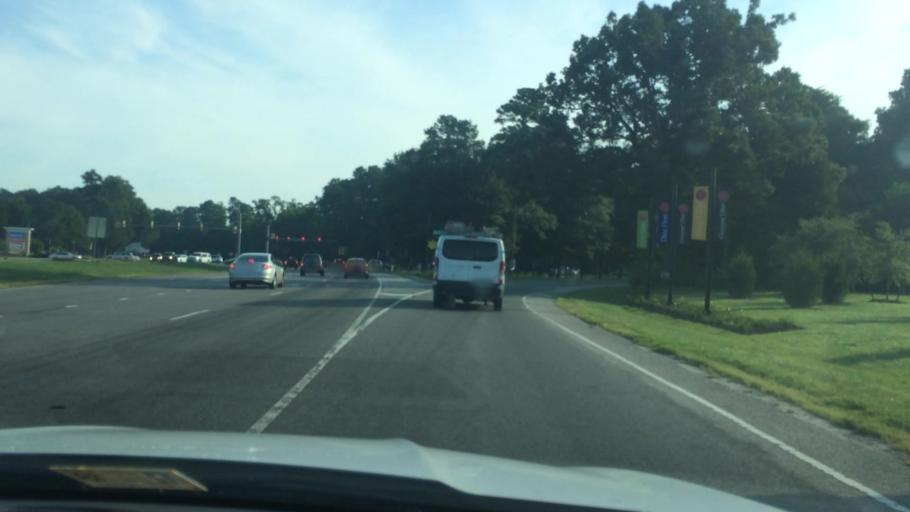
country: US
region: Virginia
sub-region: Gloucester County
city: Gloucester Courthouse
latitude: 37.3969
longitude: -76.5254
